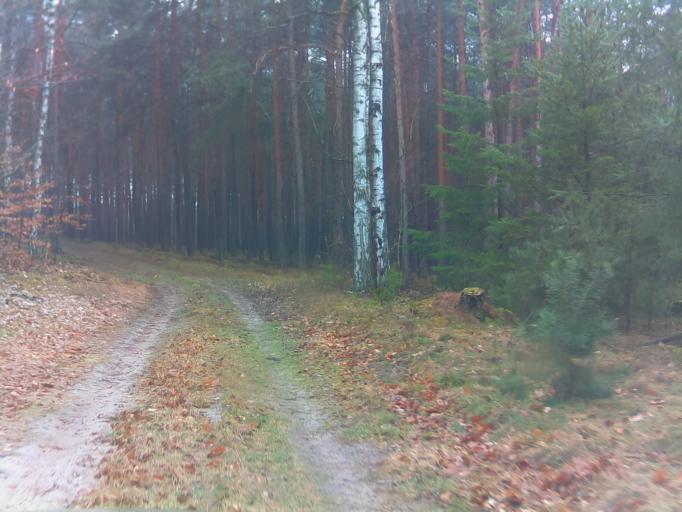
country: DE
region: Brandenburg
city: Lieberose
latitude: 52.0317
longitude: 14.3212
